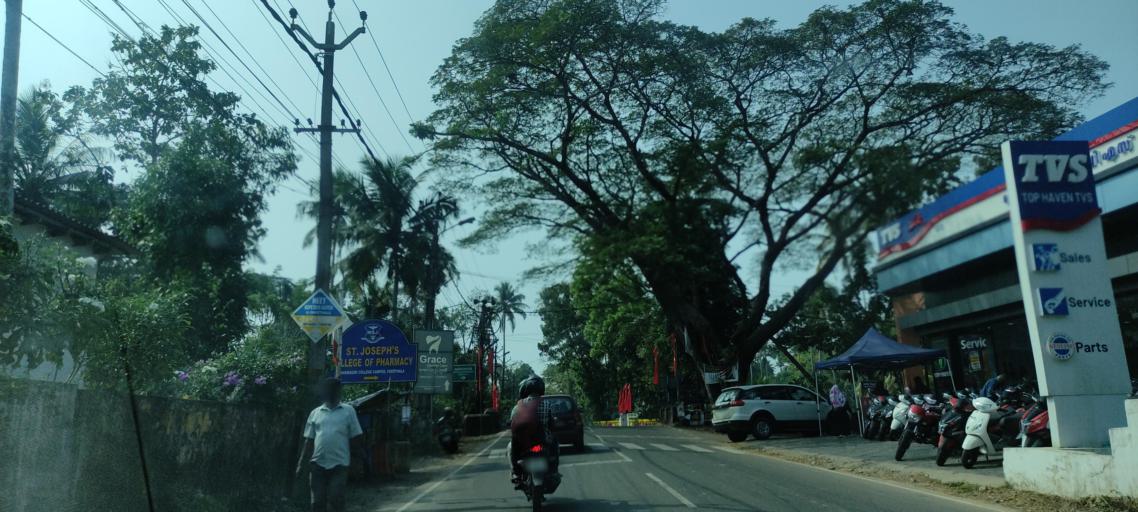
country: IN
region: Kerala
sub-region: Alappuzha
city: Vayalar
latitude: 9.6937
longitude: 76.3325
